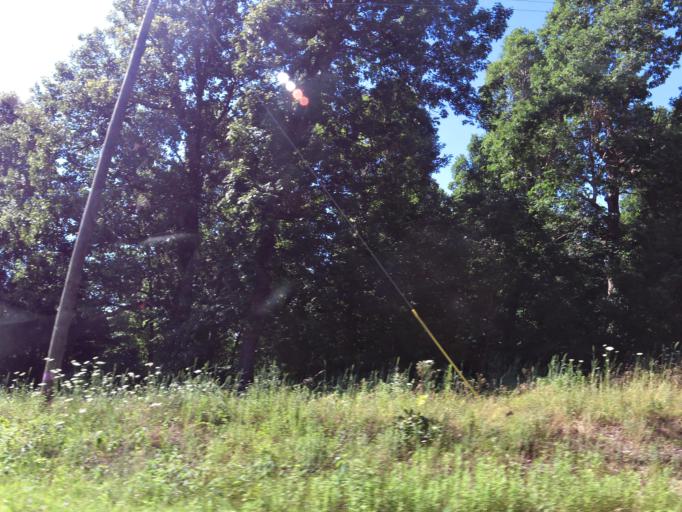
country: US
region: Arkansas
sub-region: Clay County
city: Piggott
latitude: 36.4328
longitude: -90.3052
